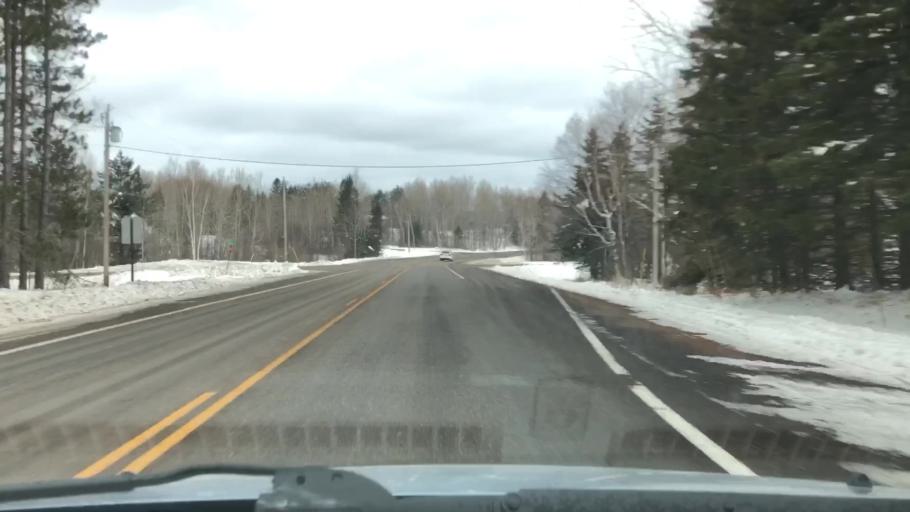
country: US
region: Minnesota
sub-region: Carlton County
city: Esko
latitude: 46.6784
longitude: -92.3734
